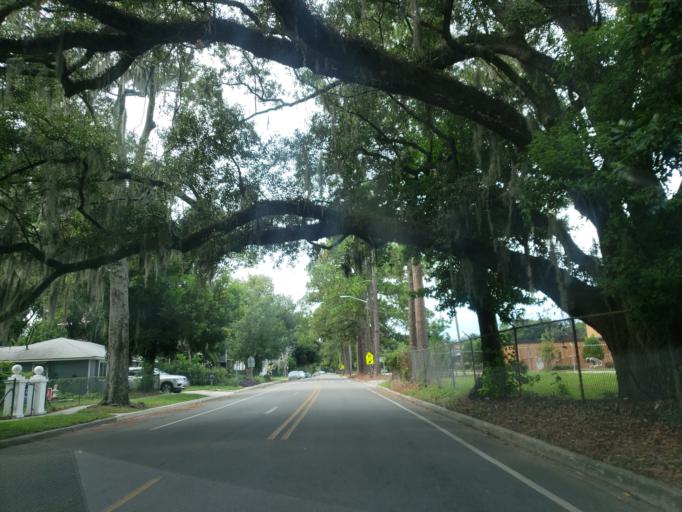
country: US
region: Georgia
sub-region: Chatham County
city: Thunderbolt
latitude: 32.0627
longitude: -81.0657
